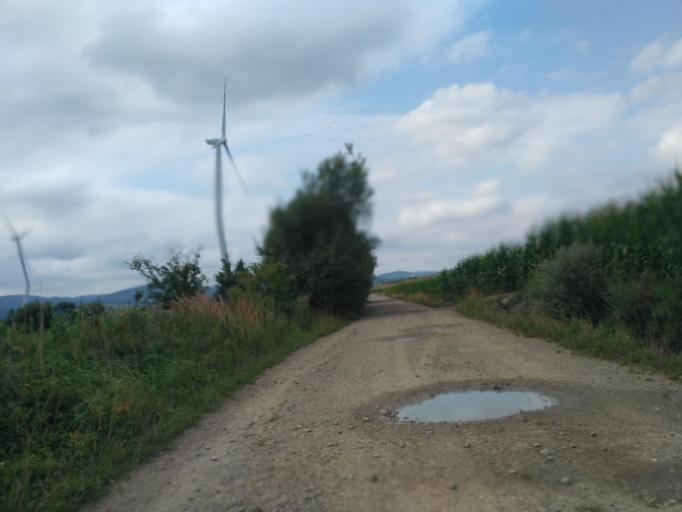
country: PL
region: Subcarpathian Voivodeship
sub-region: Powiat krosnienski
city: Rymanow
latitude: 49.6135
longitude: 21.8466
